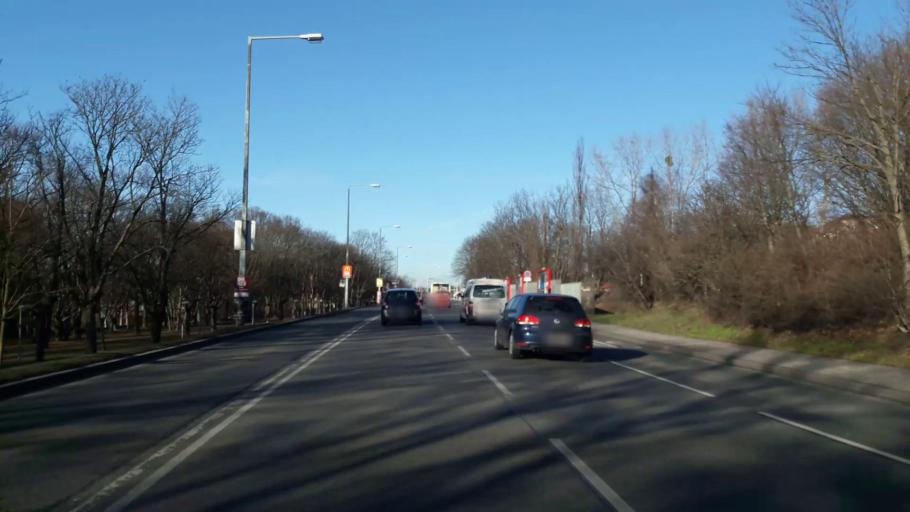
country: AT
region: Lower Austria
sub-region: Politischer Bezirk Wien-Umgebung
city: Leopoldsdorf
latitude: 48.1576
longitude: 16.3896
